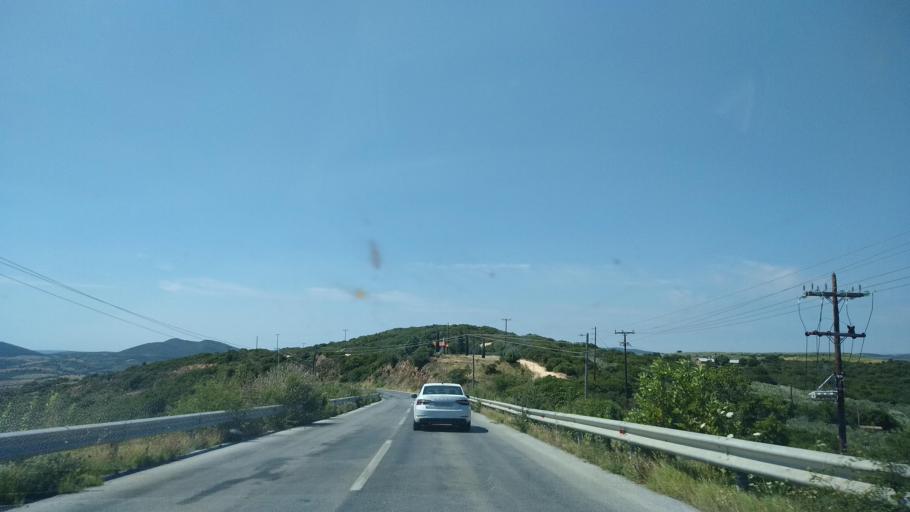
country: GR
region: Central Macedonia
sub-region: Nomos Chalkidikis
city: Megali Panagia
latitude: 40.4023
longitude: 23.6830
